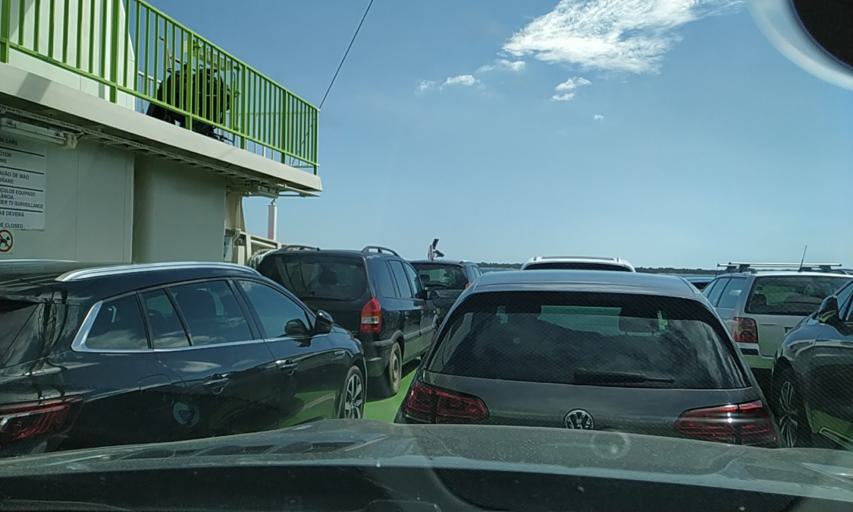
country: PT
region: Setubal
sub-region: Setubal
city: Setubal
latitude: 38.5066
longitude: -8.8850
